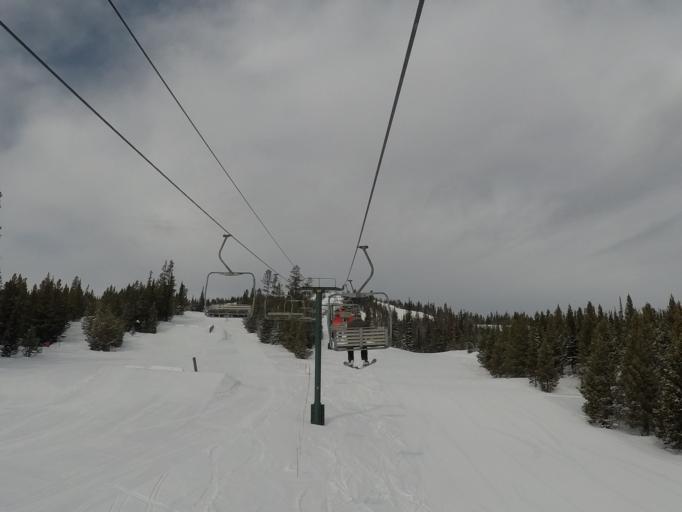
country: US
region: Montana
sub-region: Meagher County
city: White Sulphur Springs
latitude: 46.8362
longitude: -110.7027
